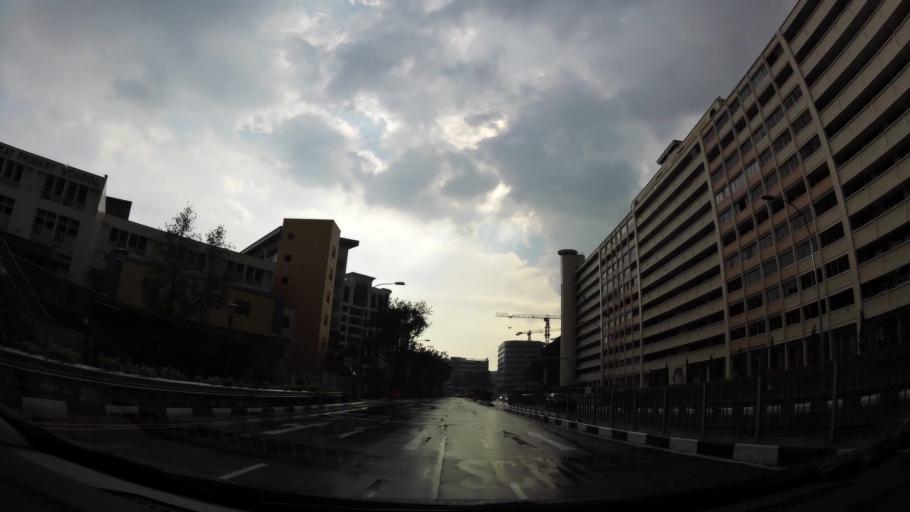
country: SG
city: Singapore
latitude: 1.3409
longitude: 103.9520
